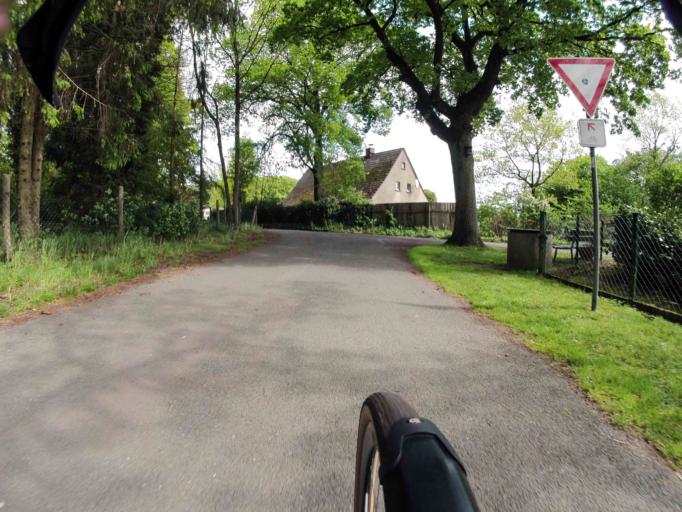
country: DE
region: North Rhine-Westphalia
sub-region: Regierungsbezirk Munster
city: Westerkappeln
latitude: 52.3318
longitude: 7.9268
